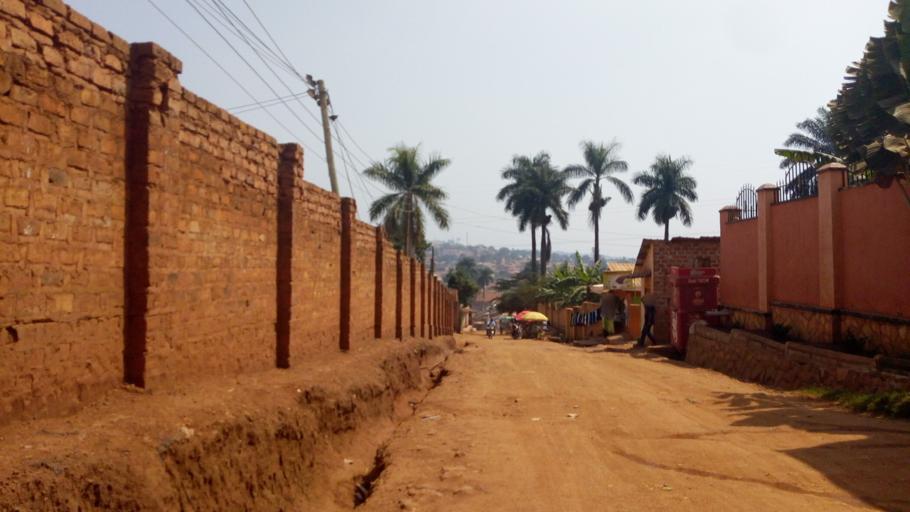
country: UG
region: Central Region
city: Kampala Central Division
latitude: 0.3464
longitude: 32.5613
